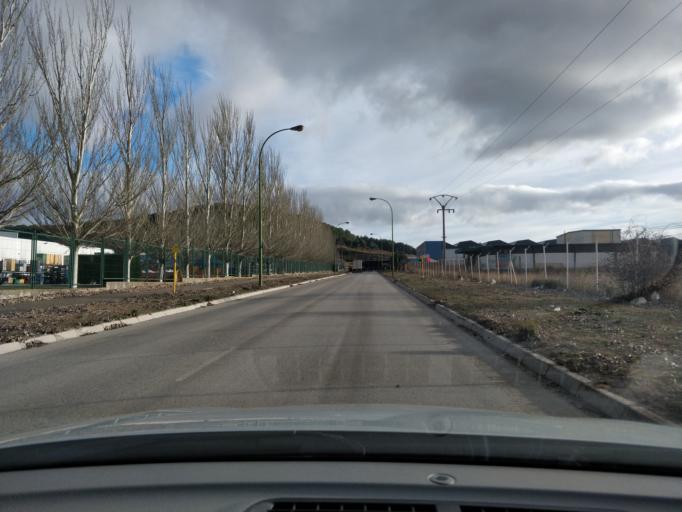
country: ES
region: Castille and Leon
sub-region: Provincia de Burgos
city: Villalbilla de Burgos
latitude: 42.3655
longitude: -3.7529
